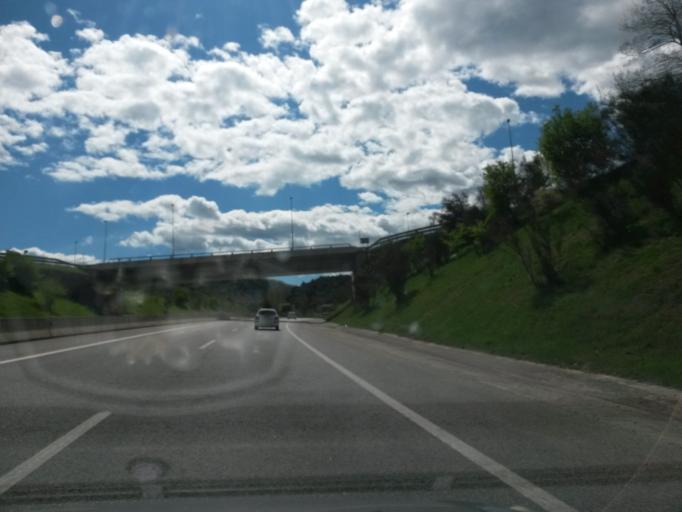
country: ES
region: Catalonia
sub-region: Provincia de Girona
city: Sant Joan les Fonts
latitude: 42.1947
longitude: 2.5260
